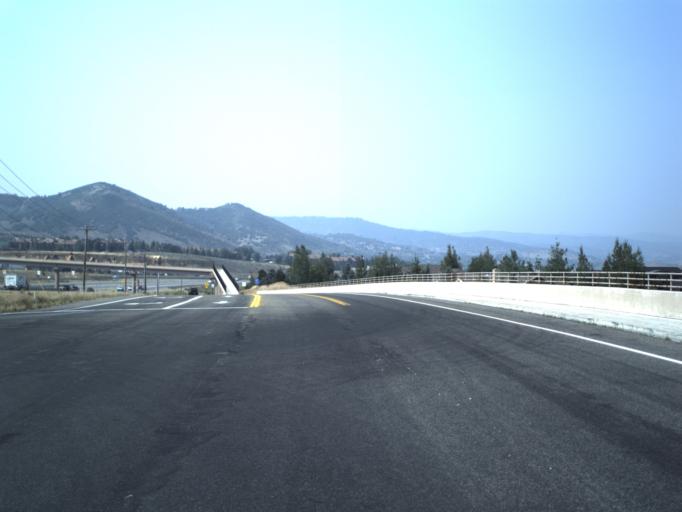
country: US
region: Utah
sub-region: Summit County
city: Snyderville
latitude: 40.7279
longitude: -111.5427
